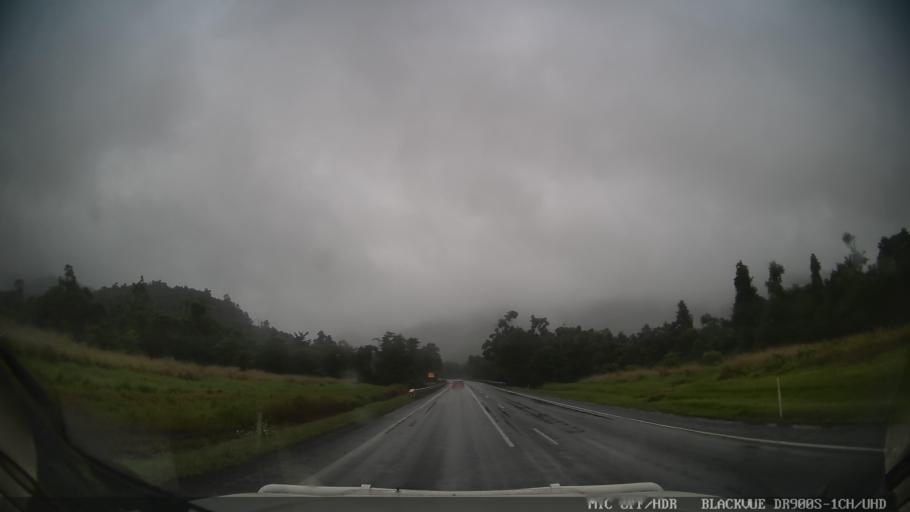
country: AU
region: Queensland
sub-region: Cassowary Coast
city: Innisfail
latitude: -17.8649
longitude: 145.9828
